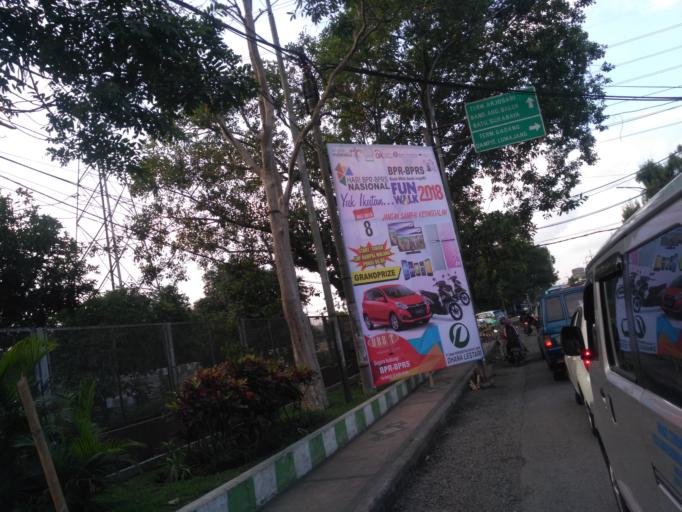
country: ID
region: East Java
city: Kebonsari
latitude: -8.0221
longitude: 112.6181
